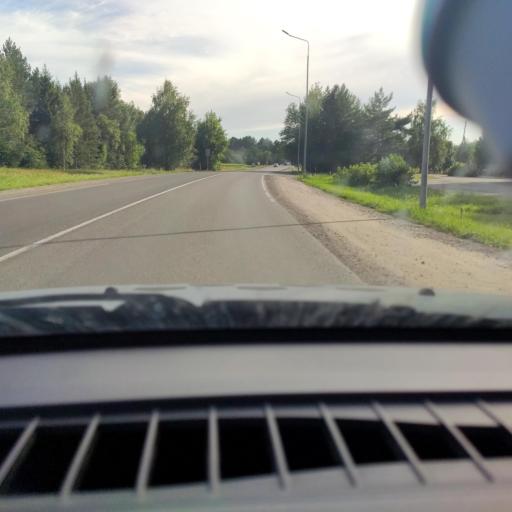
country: RU
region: Kirov
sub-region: Kirovo-Chepetskiy Rayon
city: Kirov
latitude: 58.6195
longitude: 49.7743
